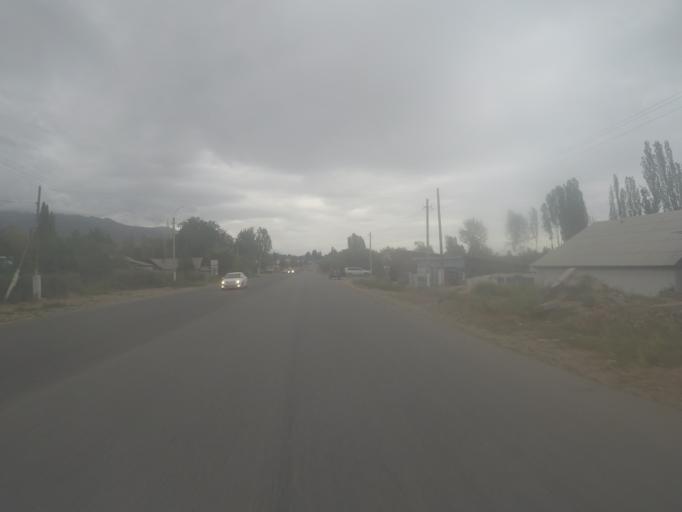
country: KG
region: Ysyk-Koel
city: Cholpon-Ata
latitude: 42.6889
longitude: 77.3499
